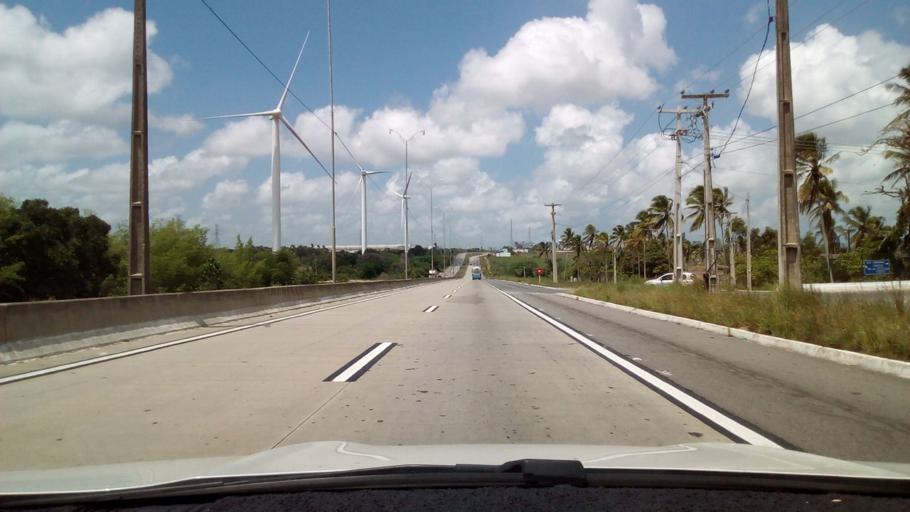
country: BR
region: Paraiba
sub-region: Conde
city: Conde
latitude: -7.2724
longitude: -34.9378
